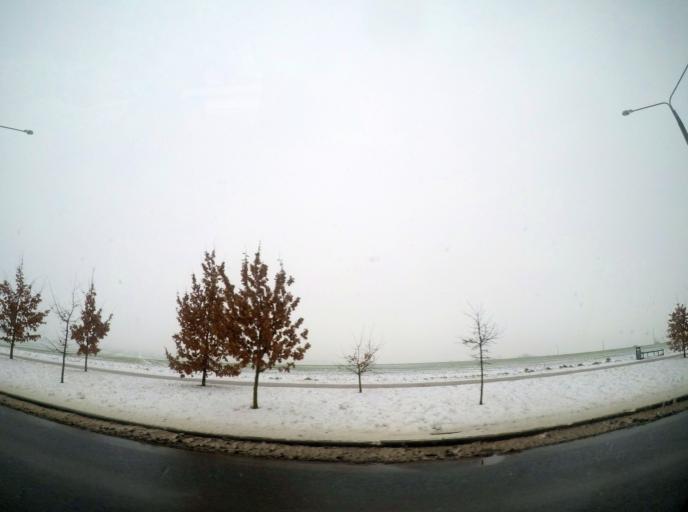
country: BY
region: Grodnenskaya
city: Hrodna
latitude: 53.6222
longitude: 23.8181
